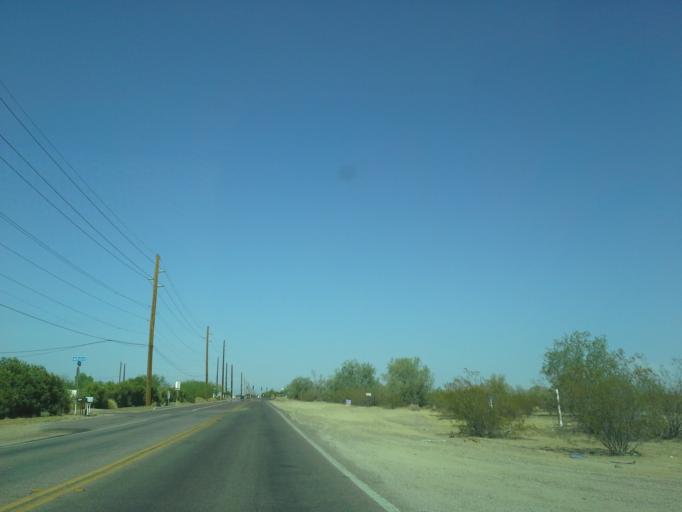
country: US
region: Arizona
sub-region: Maricopa County
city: Queen Creek
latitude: 33.2050
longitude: -111.6395
